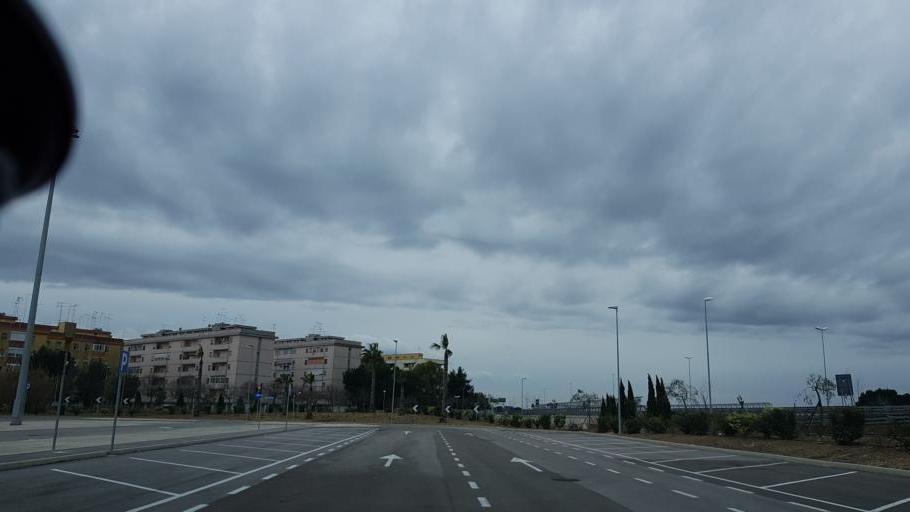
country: IT
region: Apulia
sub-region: Provincia di Brindisi
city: Brindisi
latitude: 40.6226
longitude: 17.9144
